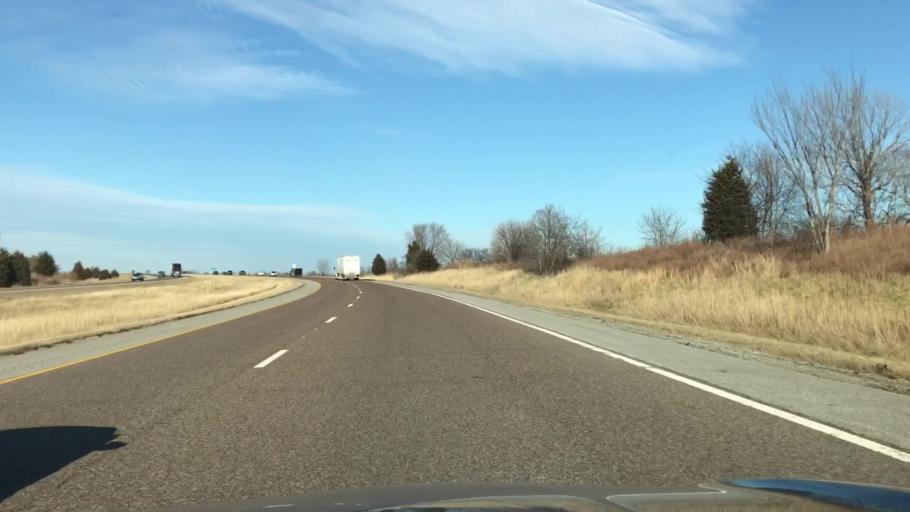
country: US
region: Illinois
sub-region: Macoupin County
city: Staunton
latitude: 38.9717
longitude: -89.7498
